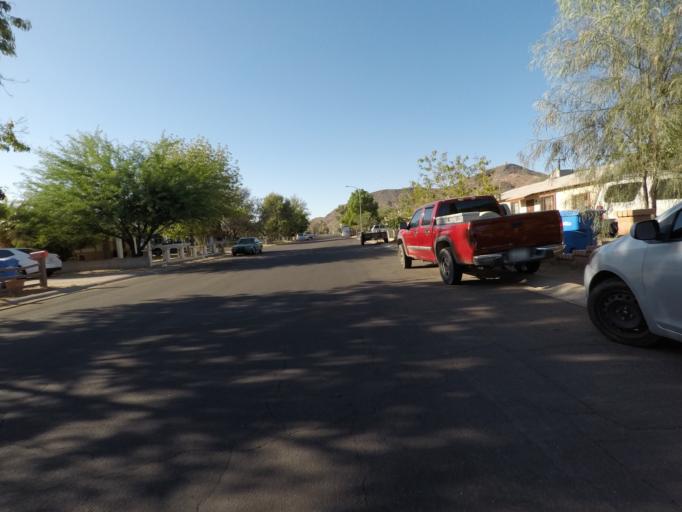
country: US
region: Arizona
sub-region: Maricopa County
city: Glendale
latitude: 33.5793
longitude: -112.0956
